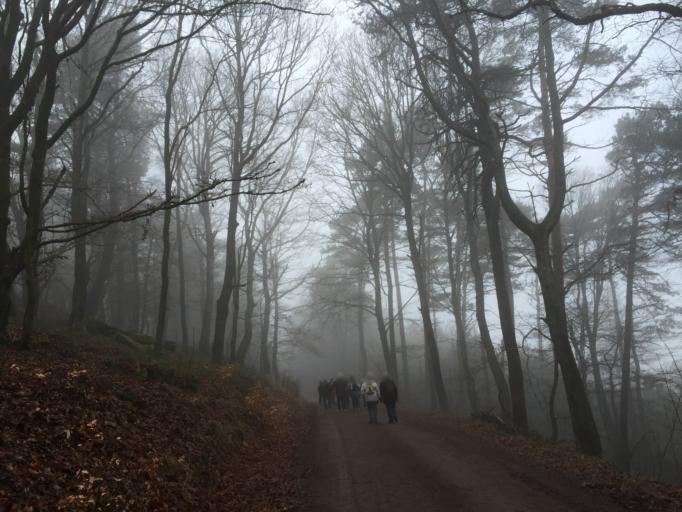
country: DE
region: Rheinland-Pfalz
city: Sankt Martin
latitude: 49.3329
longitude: 8.0956
